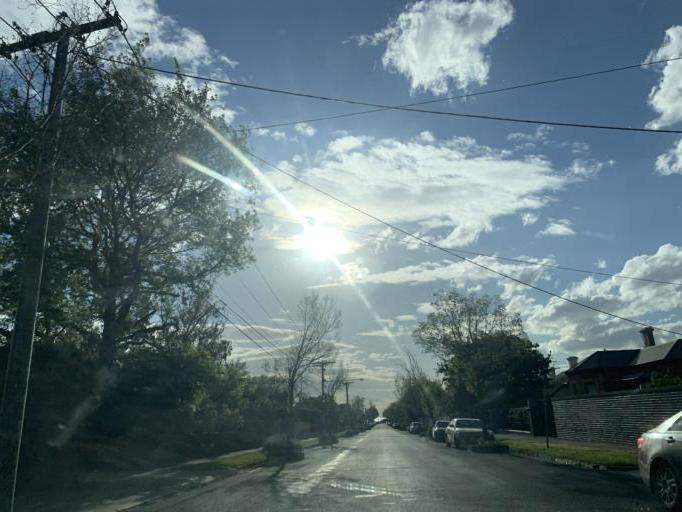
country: AU
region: Victoria
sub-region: Bayside
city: North Brighton
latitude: -37.9113
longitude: 144.9905
